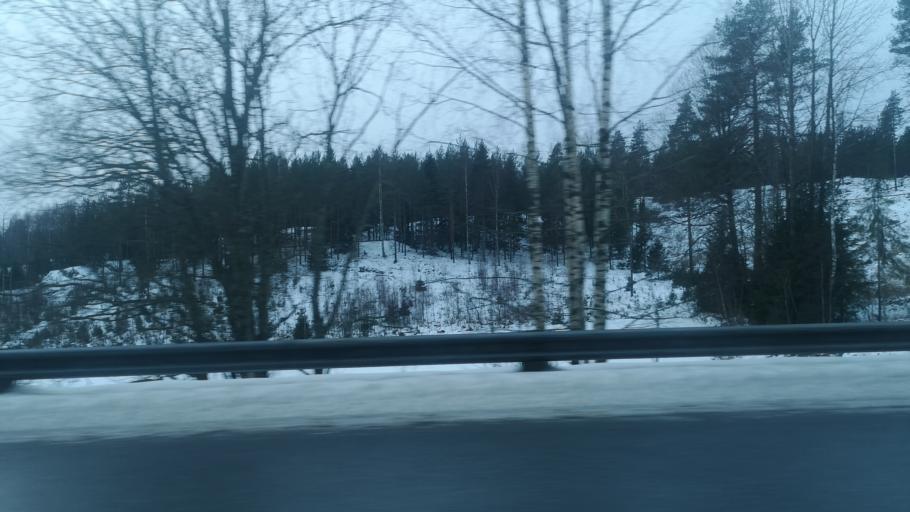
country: FI
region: Uusimaa
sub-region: Helsinki
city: Karjalohja
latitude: 60.2200
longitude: 23.6235
